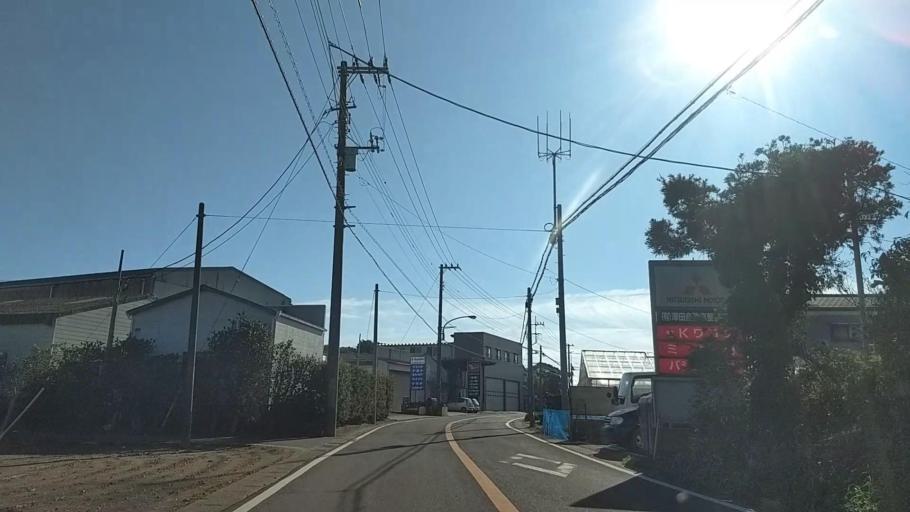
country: JP
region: Chiba
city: Hasaki
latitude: 35.7193
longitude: 140.8552
